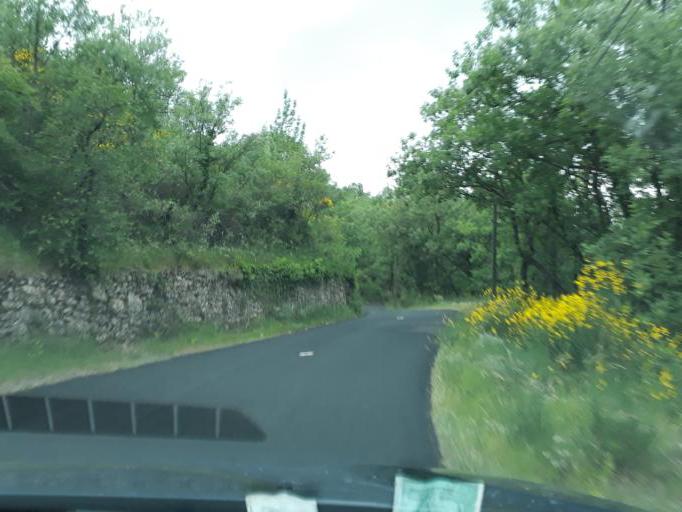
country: FR
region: Languedoc-Roussillon
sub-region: Departement de l'Herault
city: Lodeve
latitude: 43.7691
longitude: 3.3020
